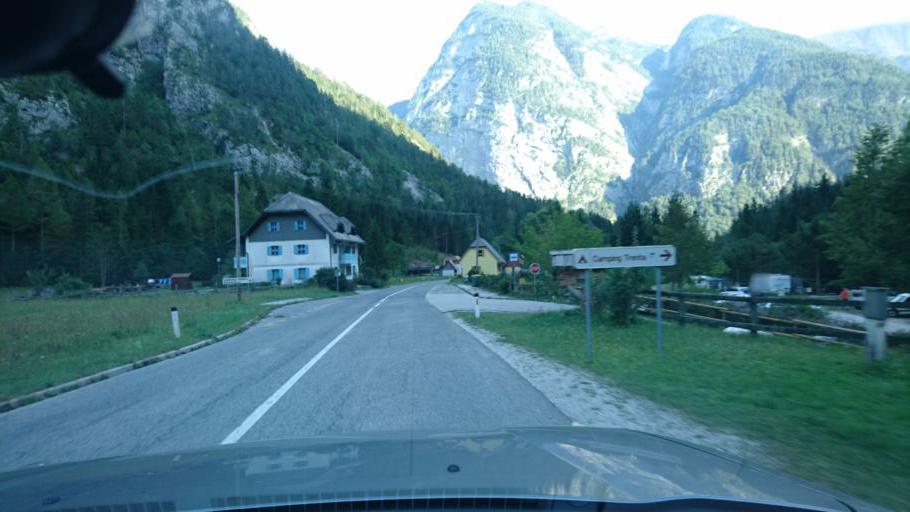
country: SI
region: Kranjska Gora
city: Kranjska Gora
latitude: 46.3892
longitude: 13.7473
